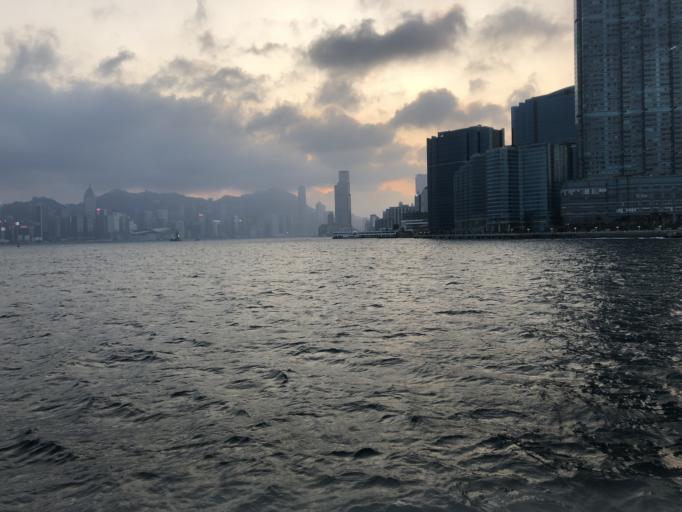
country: HK
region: Kowloon City
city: Kowloon
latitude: 22.3031
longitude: 114.1967
